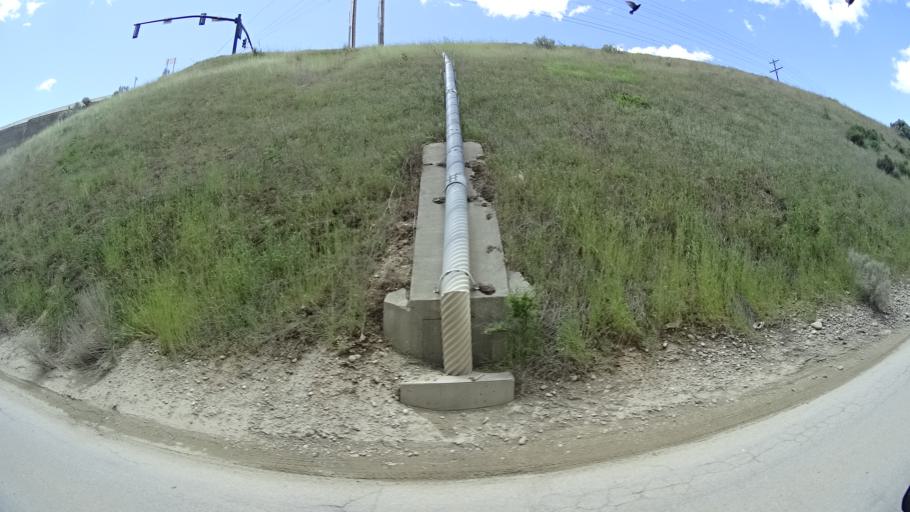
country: US
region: Idaho
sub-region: Ada County
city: Eagle
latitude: 43.6611
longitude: -116.3174
